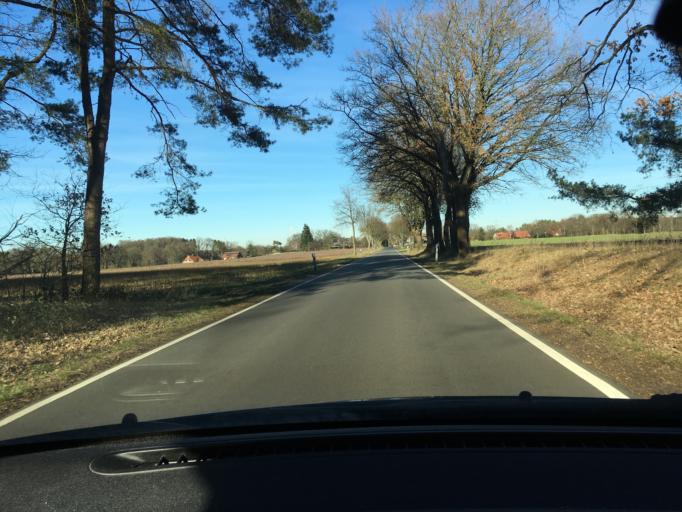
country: DE
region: Lower Saxony
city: Barnstedt
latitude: 53.1517
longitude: 10.3783
